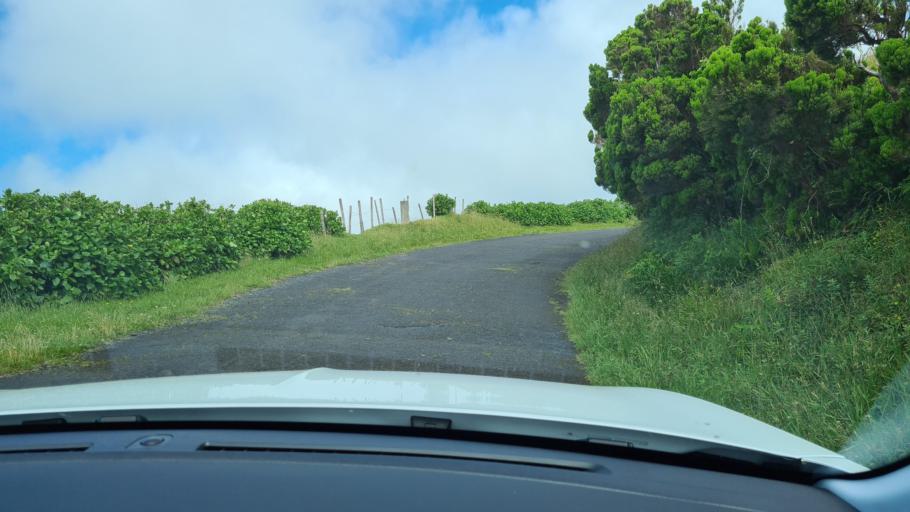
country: PT
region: Azores
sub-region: Sao Roque do Pico
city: Sao Roque do Pico
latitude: 38.6670
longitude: -28.1309
